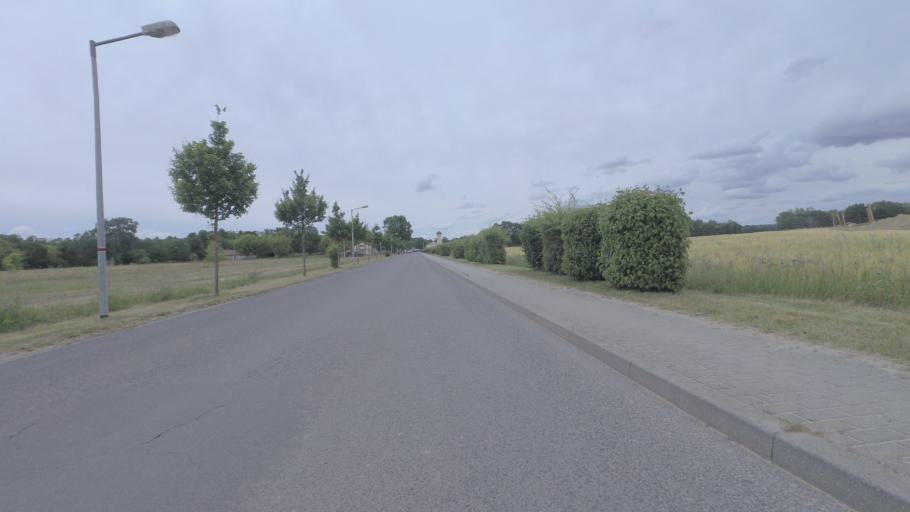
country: DE
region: Brandenburg
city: Bestensee
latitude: 52.2779
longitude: 13.7431
